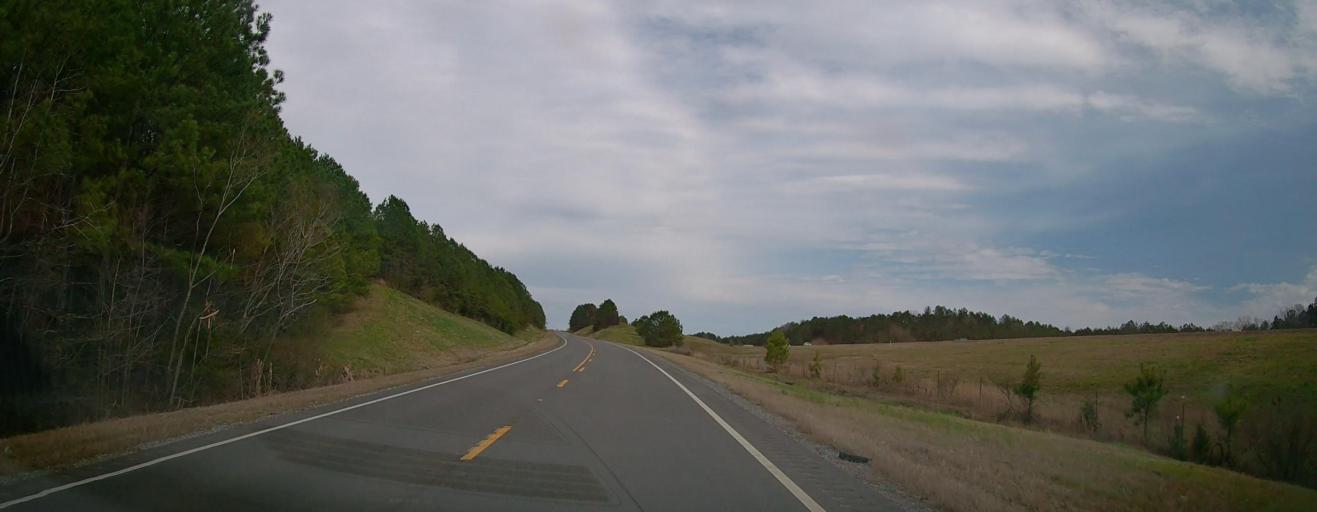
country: US
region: Alabama
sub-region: Walker County
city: Jasper
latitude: 33.8590
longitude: -87.3760
